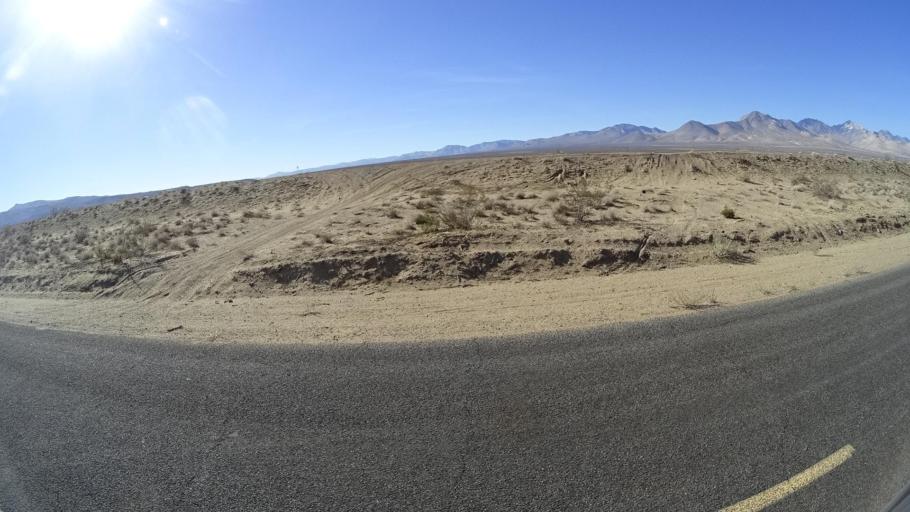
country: US
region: California
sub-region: Kern County
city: Inyokern
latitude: 35.6008
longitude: -117.7977
